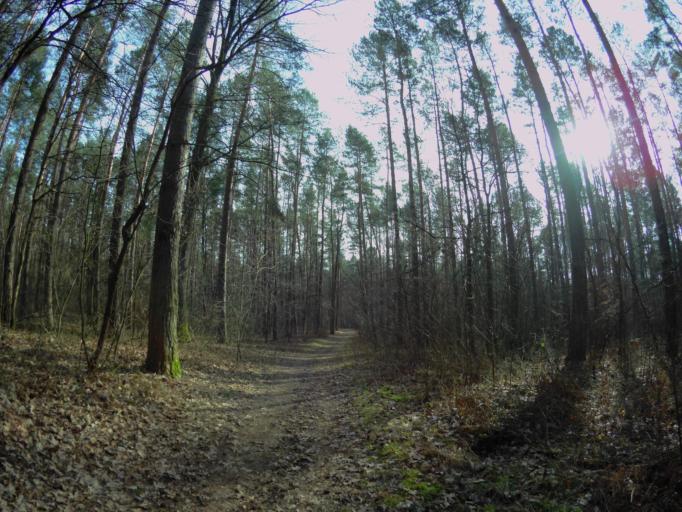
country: PL
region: Subcarpathian Voivodeship
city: Nowa Sarzyna
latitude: 50.3153
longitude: 22.3468
